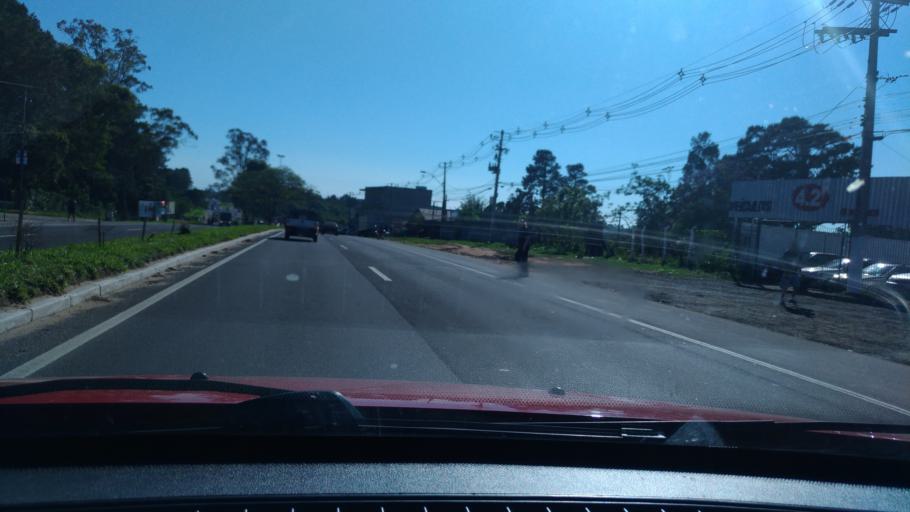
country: BR
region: Rio Grande do Sul
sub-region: Viamao
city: Viamao
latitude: -30.0898
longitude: -51.0617
